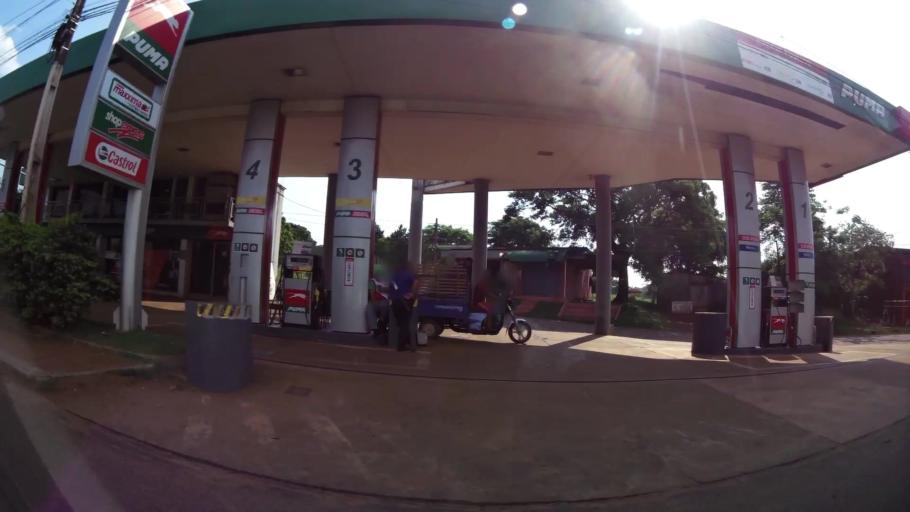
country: PY
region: Alto Parana
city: Presidente Franco
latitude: -25.5265
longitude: -54.6373
